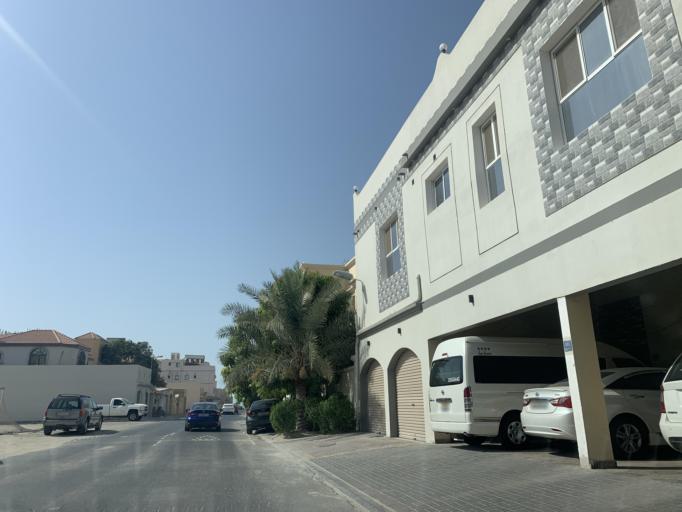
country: BH
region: Manama
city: Jidd Hafs
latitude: 26.2308
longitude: 50.4848
